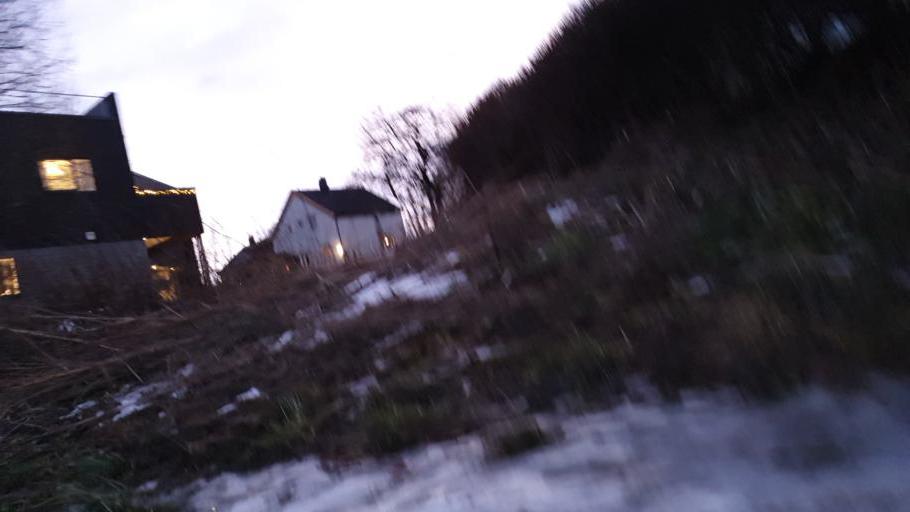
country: NO
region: Sor-Trondelag
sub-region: Trondheim
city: Trondheim
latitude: 63.4351
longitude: 10.5105
